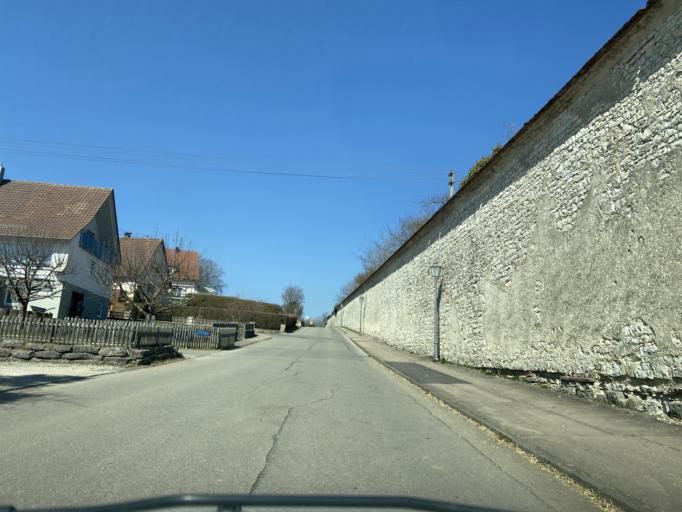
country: DE
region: Baden-Wuerttemberg
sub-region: Tuebingen Region
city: Inzigkofen
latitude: 48.0730
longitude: 9.1757
